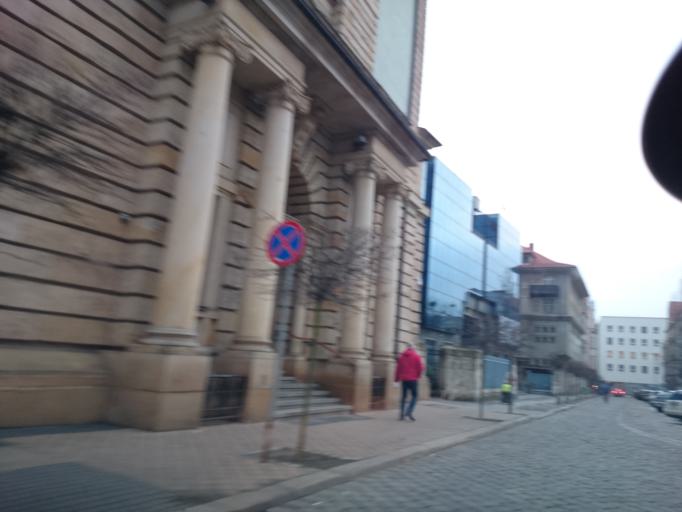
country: PL
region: Opole Voivodeship
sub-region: Powiat opolski
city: Opole
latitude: 50.6648
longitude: 17.9273
